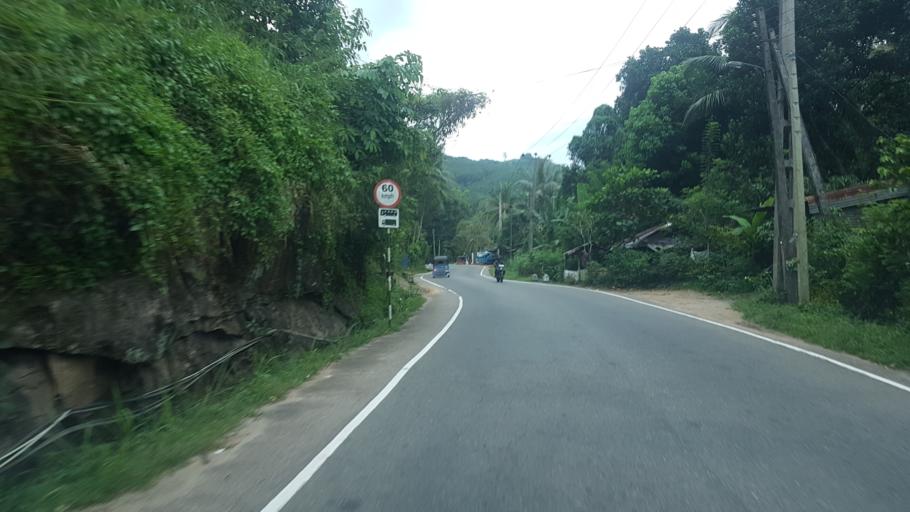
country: LK
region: Western
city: Hanwella Ihala
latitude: 7.0237
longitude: 80.2664
